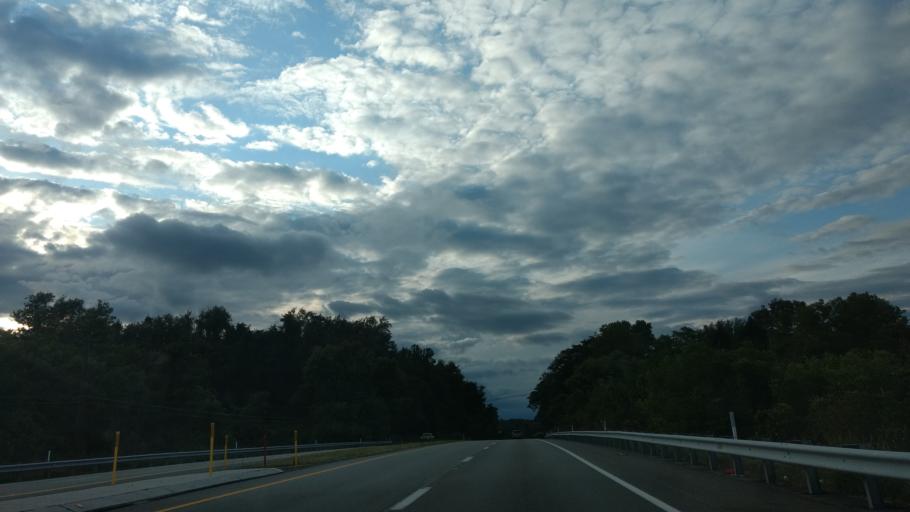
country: US
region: Pennsylvania
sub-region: Westmoreland County
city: Fellsburg
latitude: 40.1735
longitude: -79.7998
